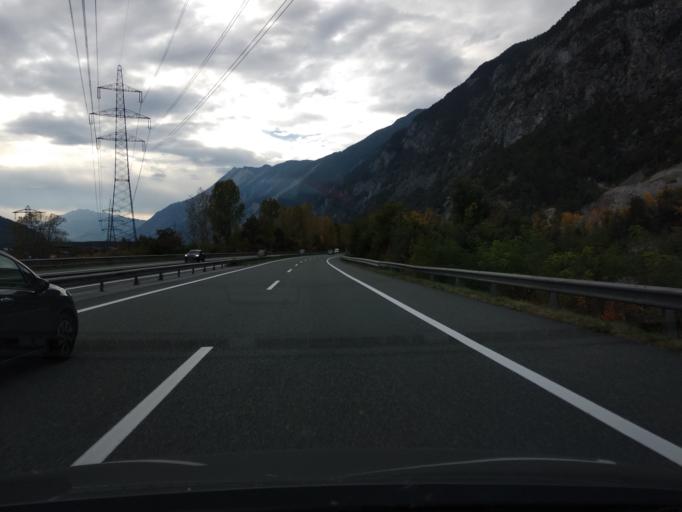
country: AT
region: Tyrol
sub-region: Politischer Bezirk Imst
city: Silz
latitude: 47.2732
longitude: 10.9356
